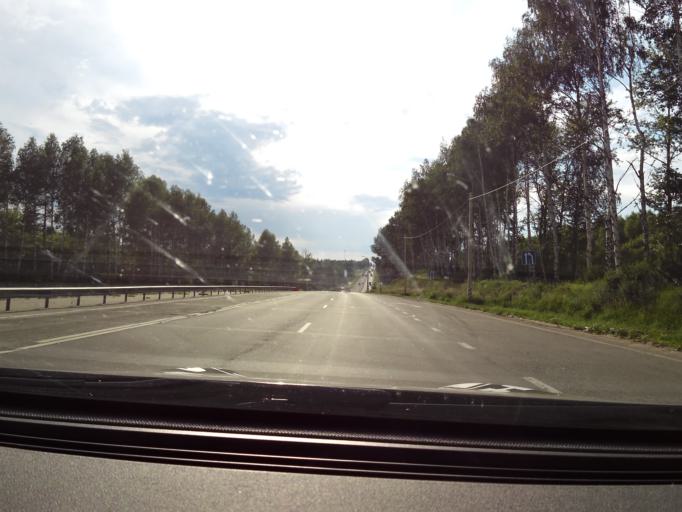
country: RU
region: Vladimir
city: Gorokhovets
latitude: 56.1674
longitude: 42.4643
